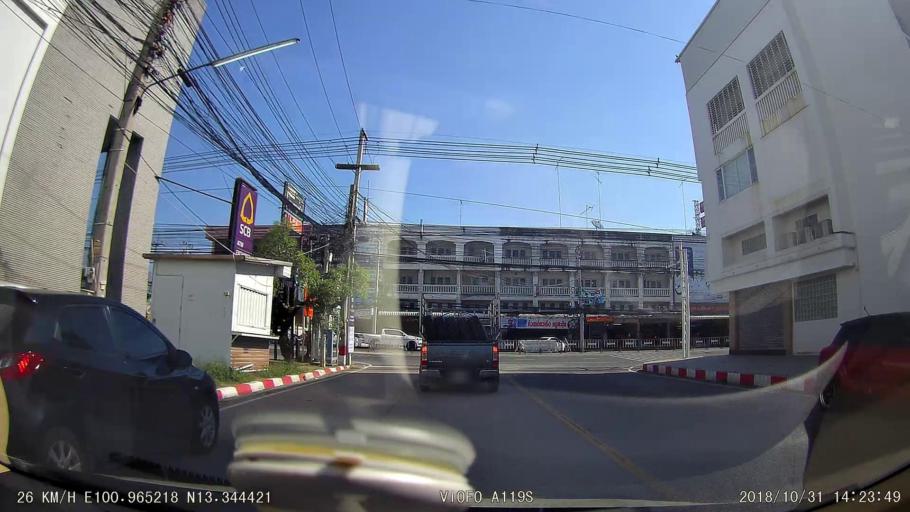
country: TH
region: Chon Buri
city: Chon Buri
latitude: 13.3443
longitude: 100.9653
